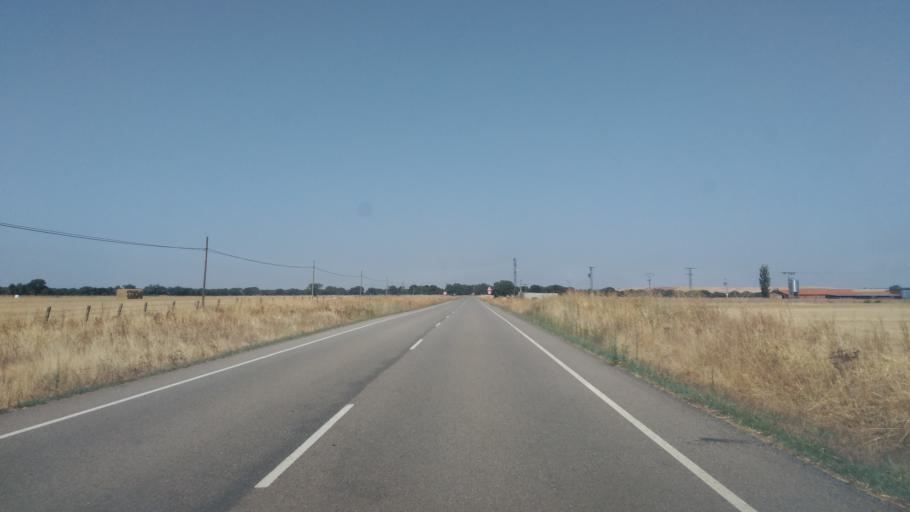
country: ES
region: Castille and Leon
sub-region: Provincia de Salamanca
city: Abusejo
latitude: 40.7194
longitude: -6.1489
